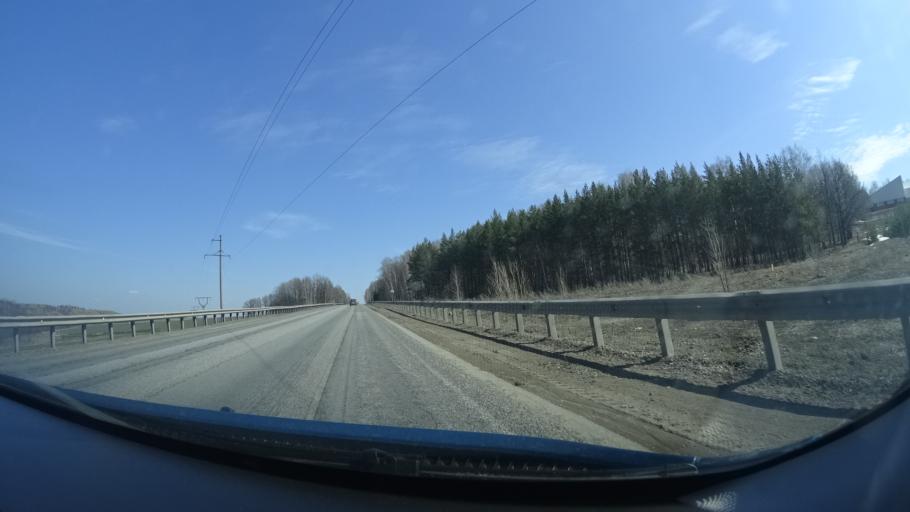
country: RU
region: Bashkortostan
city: Nizhnetroitskiy
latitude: 54.4511
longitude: 53.6333
